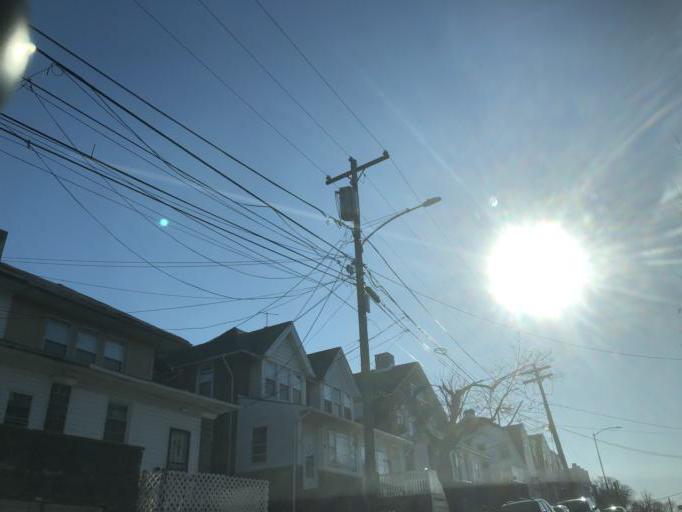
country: US
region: Pennsylvania
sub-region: Delaware County
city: Millbourne
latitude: 39.9635
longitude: -75.2530
